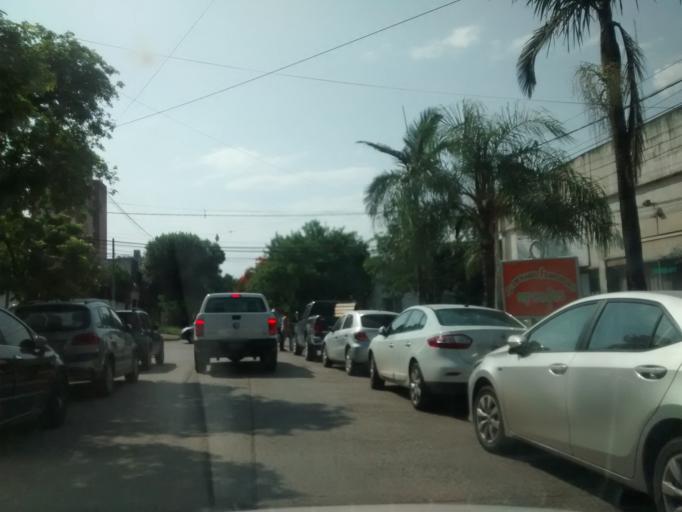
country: AR
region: Chaco
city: Resistencia
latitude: -27.4589
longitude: -58.9795
